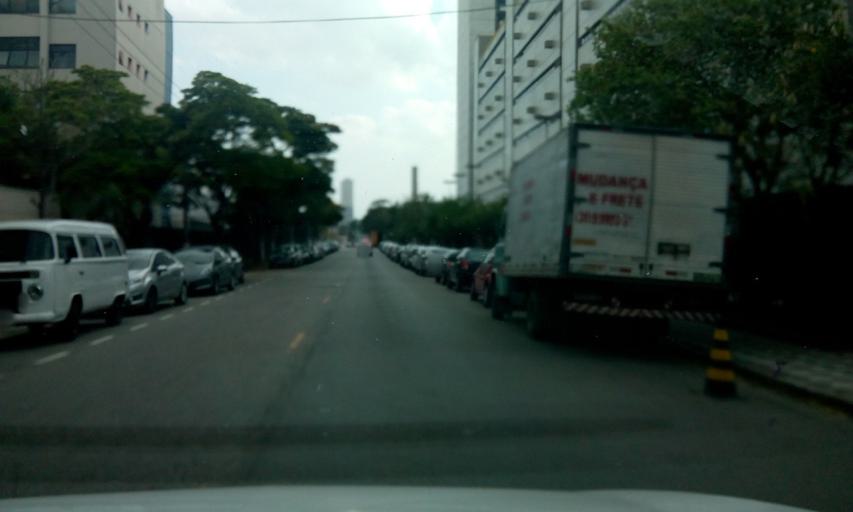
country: BR
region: Sao Paulo
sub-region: Osasco
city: Osasco
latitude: -23.5274
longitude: -46.7361
